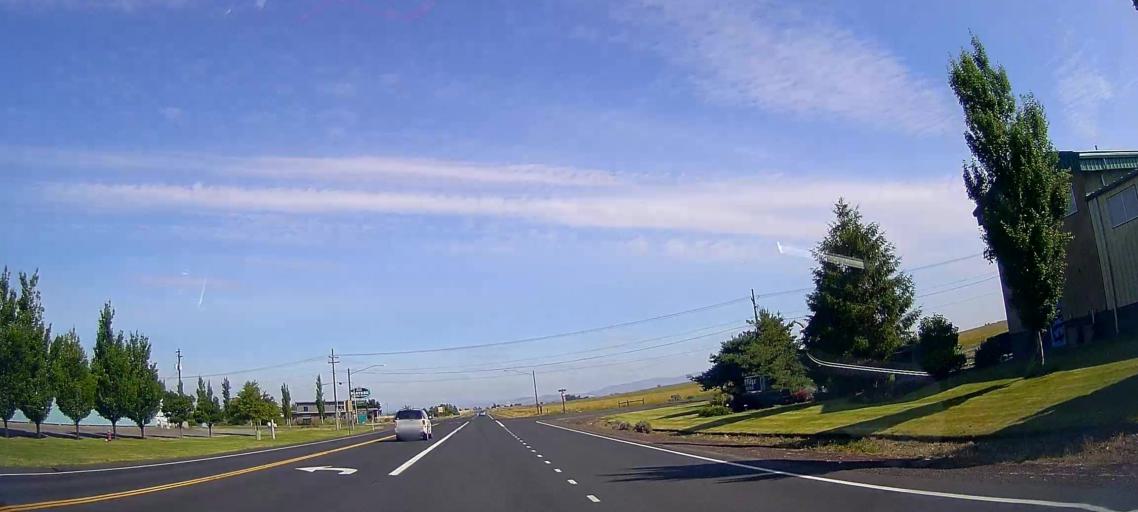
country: US
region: Oregon
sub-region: Jefferson County
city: Madras
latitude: 44.6640
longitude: -121.1353
